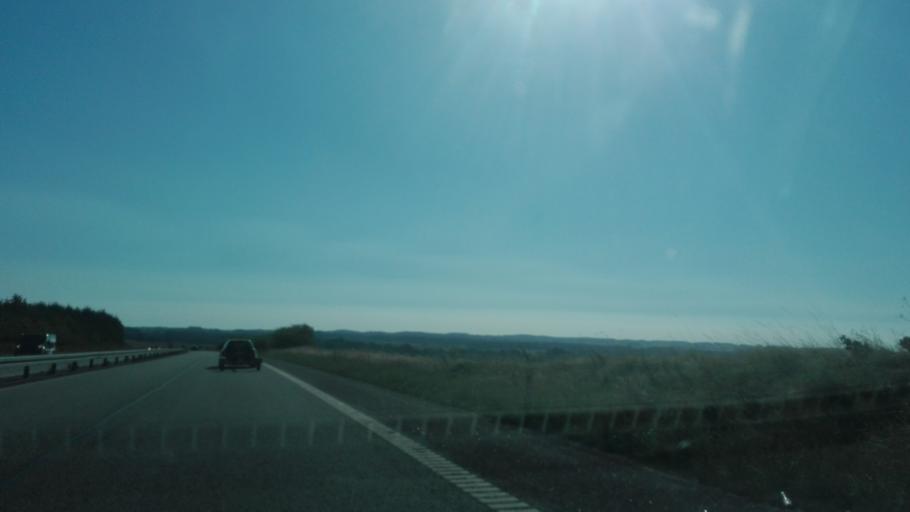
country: DK
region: Central Jutland
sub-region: Syddjurs Kommune
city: Ronde
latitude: 56.2967
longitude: 10.5189
